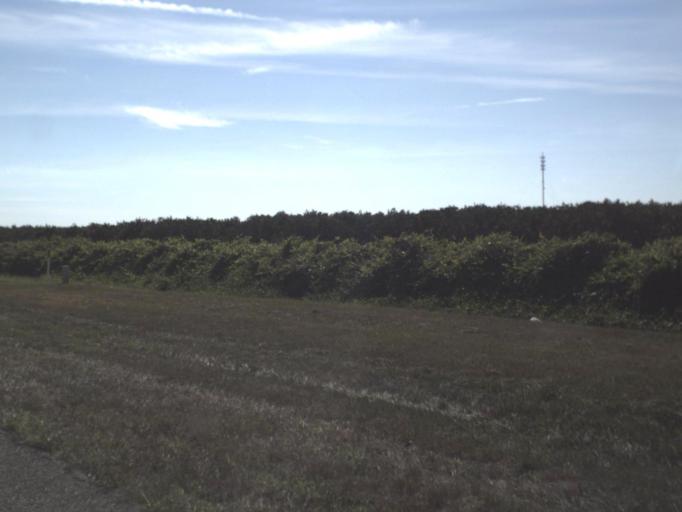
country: US
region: Florida
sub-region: Highlands County
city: Placid Lakes
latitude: 27.0738
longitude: -81.3360
